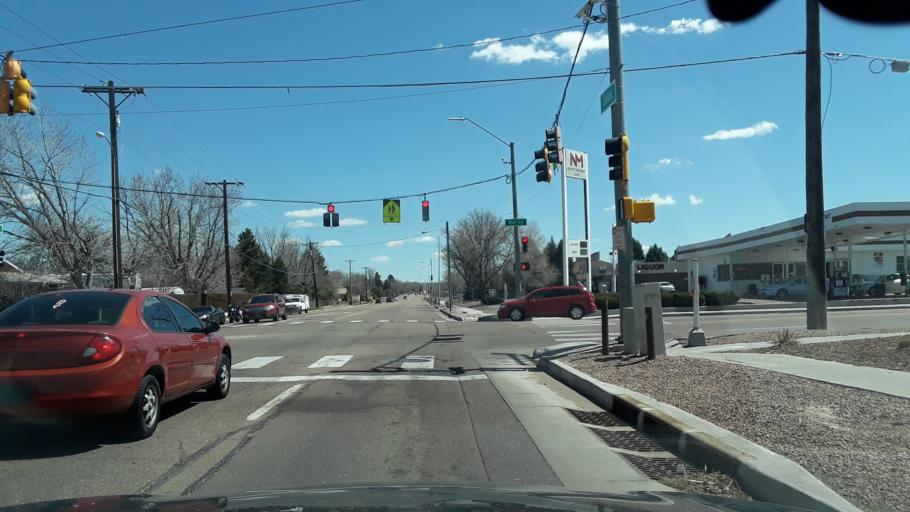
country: US
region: Colorado
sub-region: El Paso County
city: Cimarron Hills
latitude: 38.8471
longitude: -104.7483
